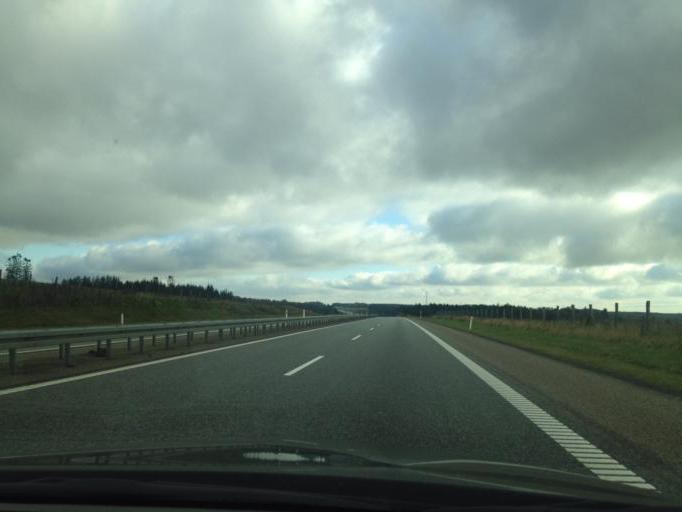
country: DK
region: South Denmark
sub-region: Vejle Kommune
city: Give
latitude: 55.8342
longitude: 9.3239
